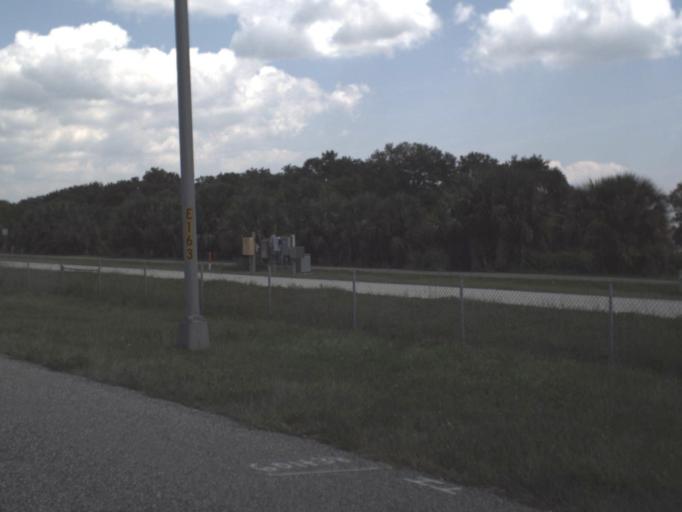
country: US
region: Florida
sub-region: Pinellas County
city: Tierra Verde
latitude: 27.6788
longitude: -82.6780
